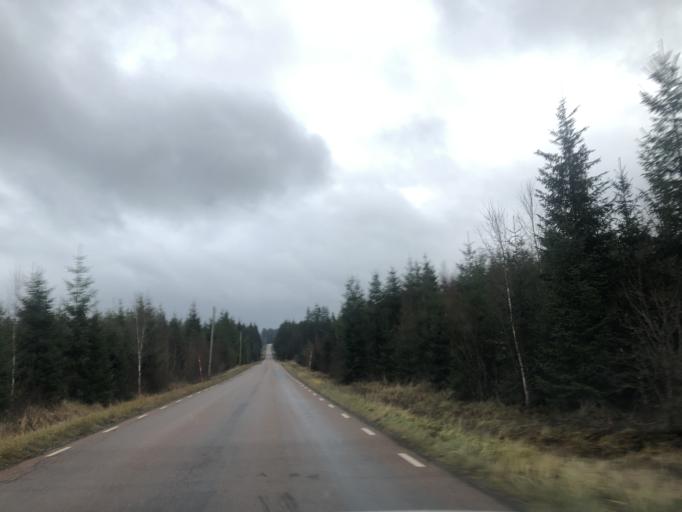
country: SE
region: Vaestra Goetaland
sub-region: Ulricehamns Kommun
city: Ulricehamn
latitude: 57.8284
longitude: 13.5047
